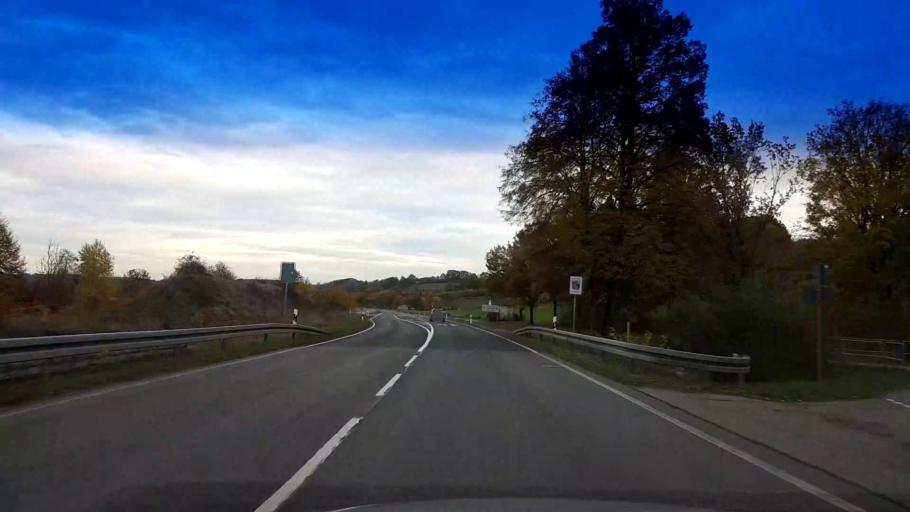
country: DE
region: Bavaria
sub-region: Regierungsbezirk Unterfranken
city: Stettfeld
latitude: 49.9378
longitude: 10.7322
